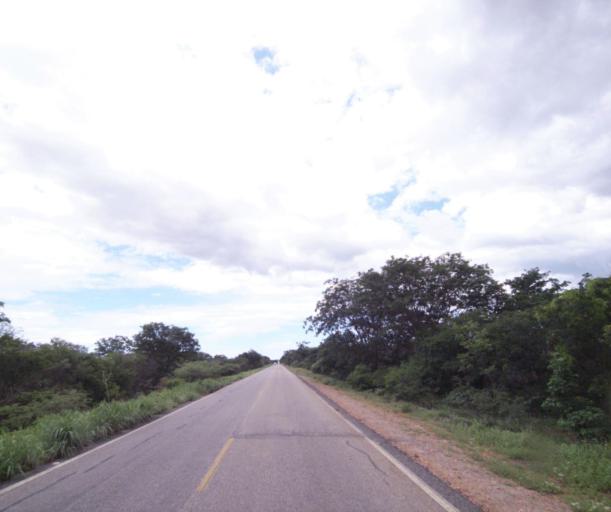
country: BR
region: Bahia
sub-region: Palmas De Monte Alto
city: Palmas de Monte Alto
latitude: -14.2615
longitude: -43.3090
